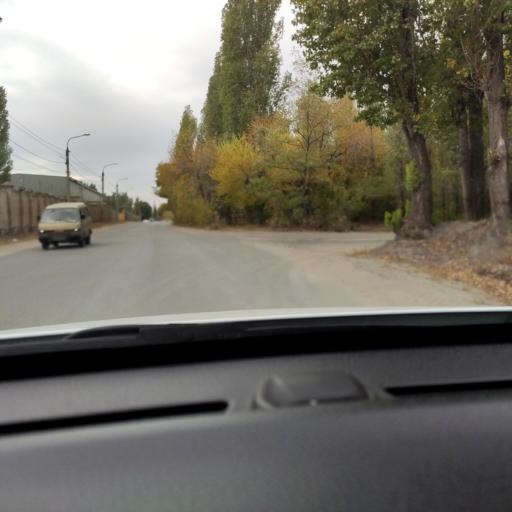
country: RU
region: Voronezj
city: Maslovka
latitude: 51.6016
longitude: 39.2625
